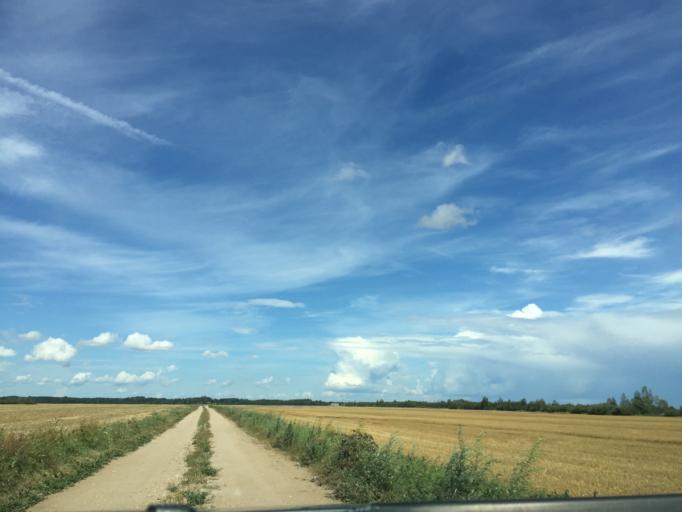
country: LT
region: Siauliu apskritis
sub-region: Joniskis
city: Joniskis
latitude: 56.3185
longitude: 23.6282
